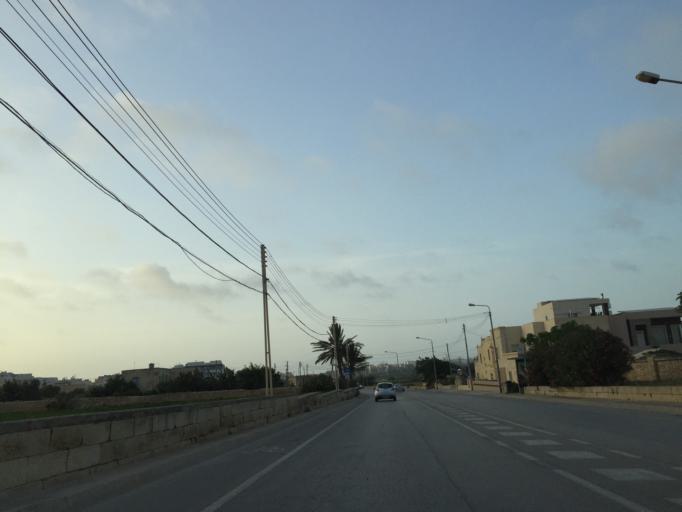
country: MT
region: Saint Paul's Bay
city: San Pawl il-Bahar
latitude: 35.9293
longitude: 14.4163
